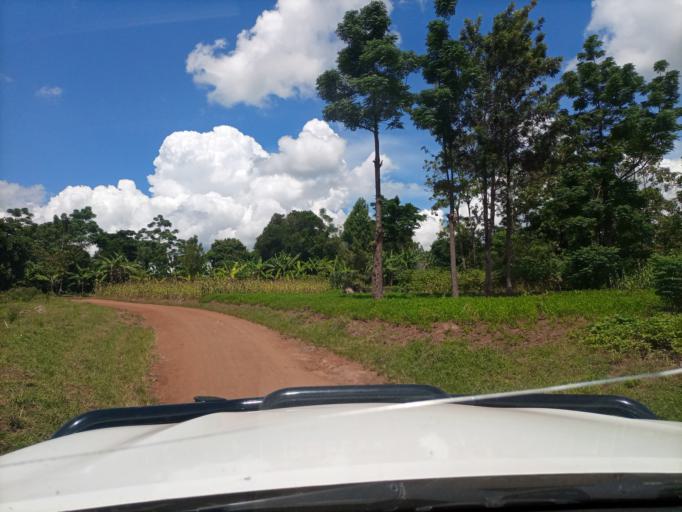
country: UG
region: Eastern Region
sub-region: Tororo District
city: Tororo
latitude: 0.6959
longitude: 34.0114
